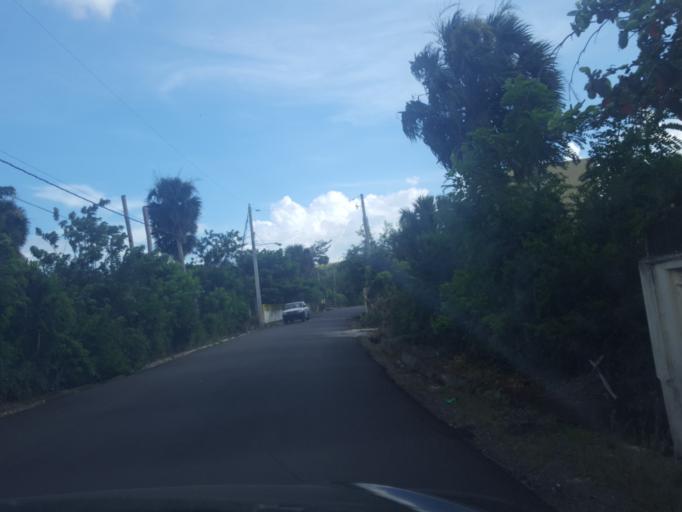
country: DO
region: Santiago
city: Baitoa
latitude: 19.3610
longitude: -70.6328
